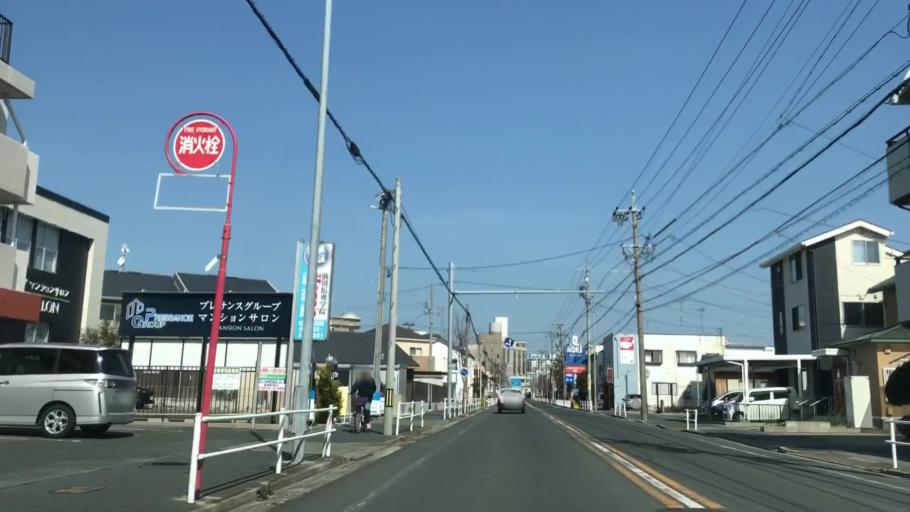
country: JP
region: Aichi
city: Toyohashi
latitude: 34.7542
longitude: 137.3797
